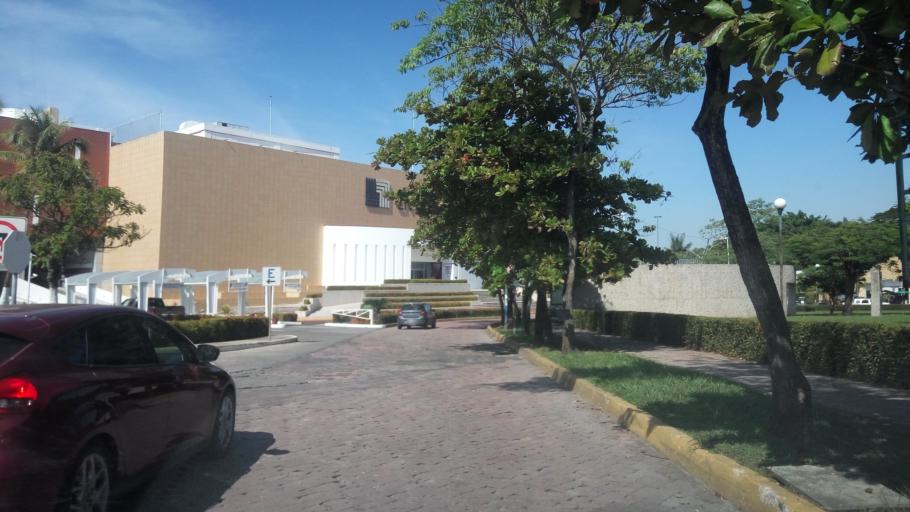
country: MX
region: Tabasco
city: Villahermosa
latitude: 17.9997
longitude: -92.9444
